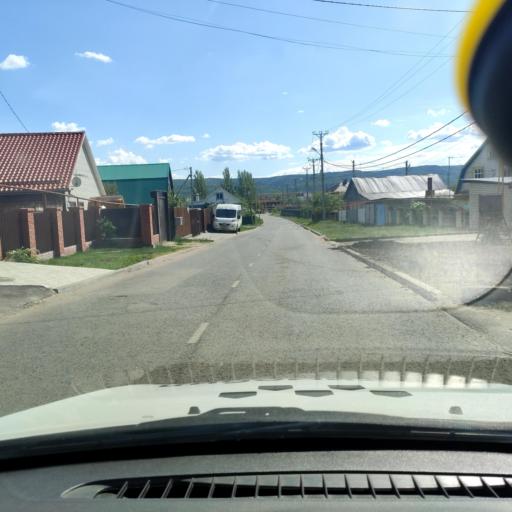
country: RU
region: Samara
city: Zhigulevsk
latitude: 53.4689
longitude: 49.6320
